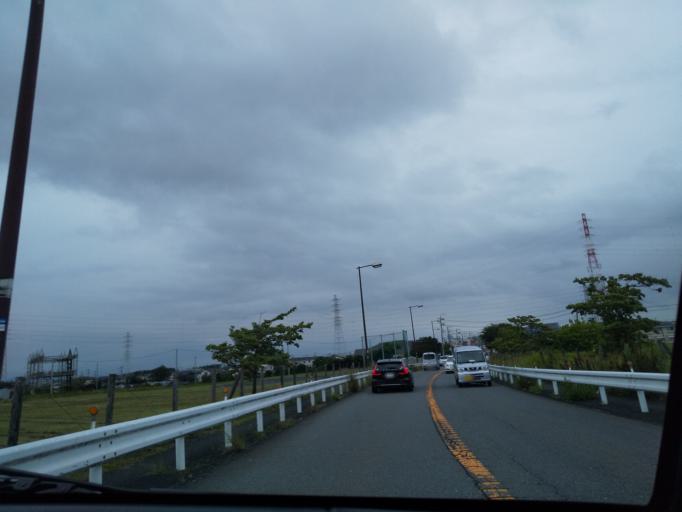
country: JP
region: Kanagawa
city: Fujisawa
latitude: 35.4009
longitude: 139.5021
